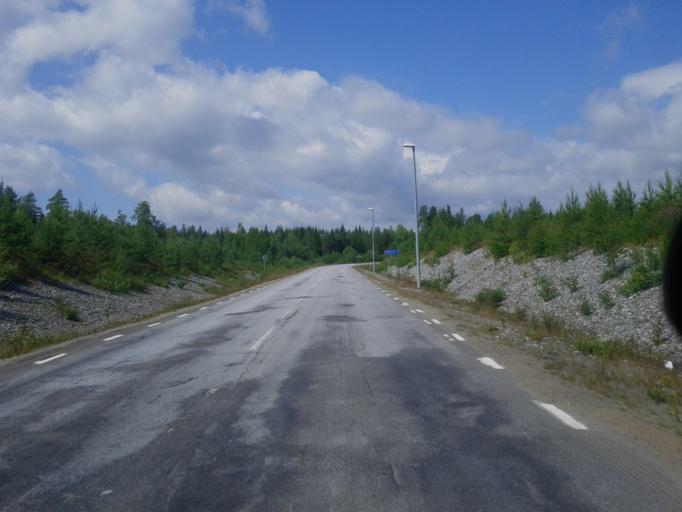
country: SE
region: Vaesterbotten
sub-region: Nordmalings Kommun
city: Nordmaling
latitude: 63.5791
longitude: 19.4609
